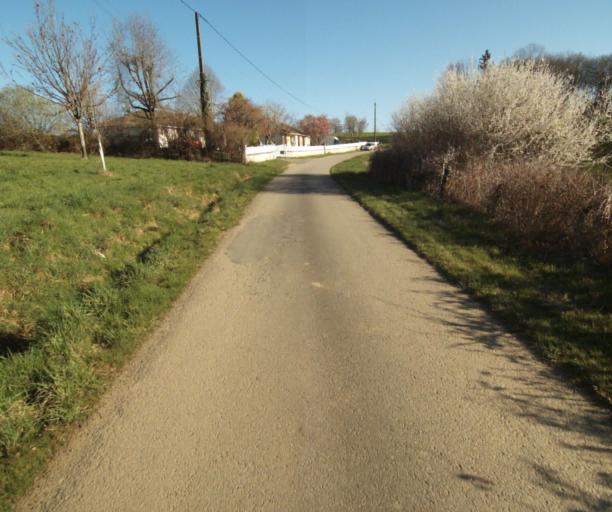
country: FR
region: Limousin
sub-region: Departement de la Correze
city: Saint-Clement
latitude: 45.3763
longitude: 1.6249
